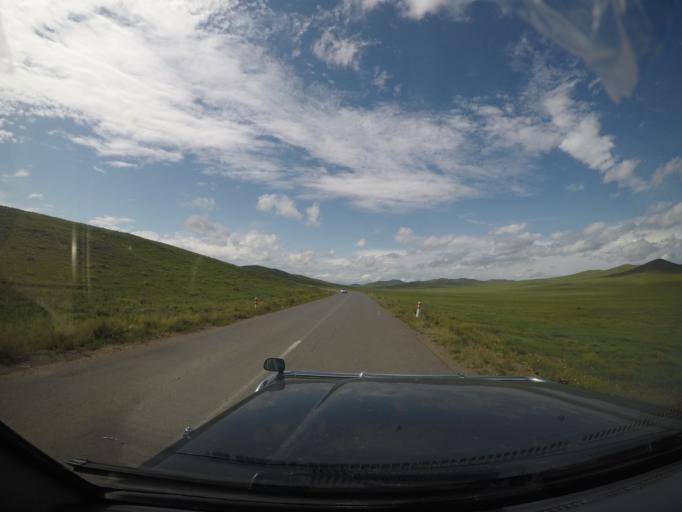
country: MN
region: Hentiy
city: Bayanbulag
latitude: 47.4547
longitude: 109.8238
